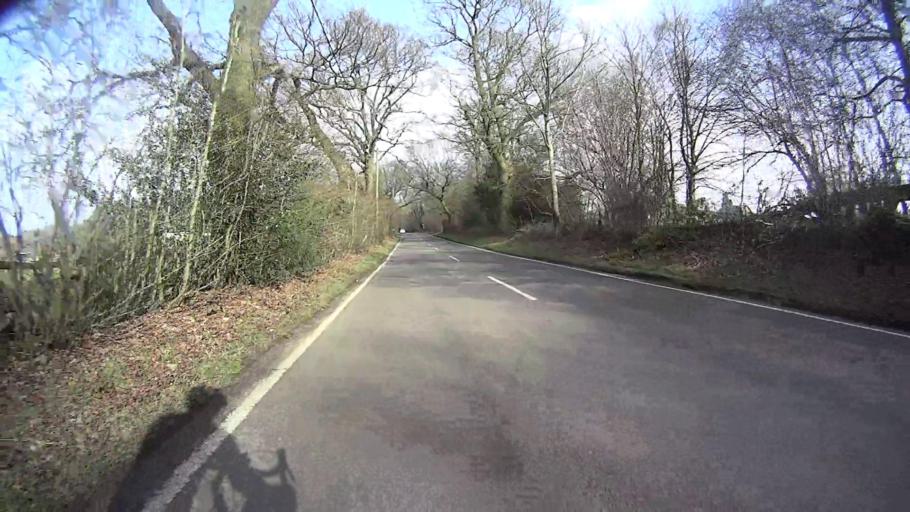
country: GB
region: England
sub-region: Surrey
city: Headley
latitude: 51.2553
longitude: -0.2751
